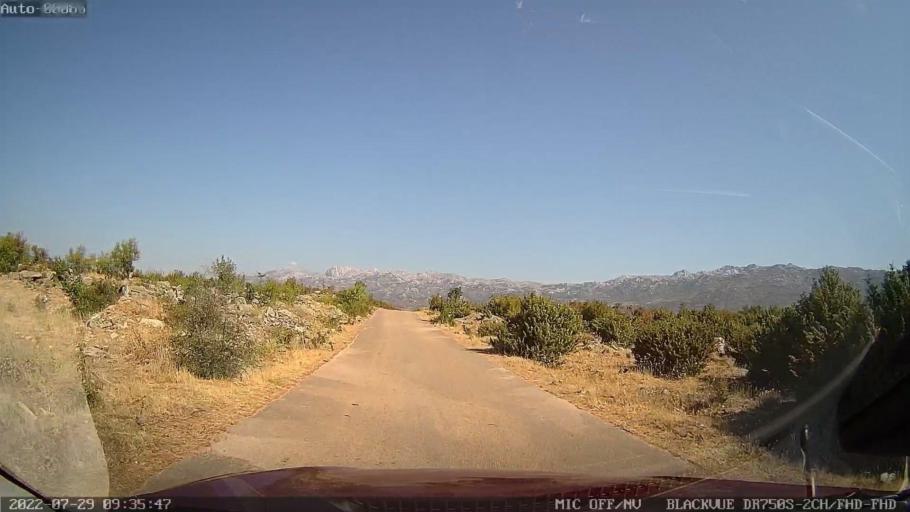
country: HR
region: Zadarska
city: Obrovac
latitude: 44.1882
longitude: 15.7331
